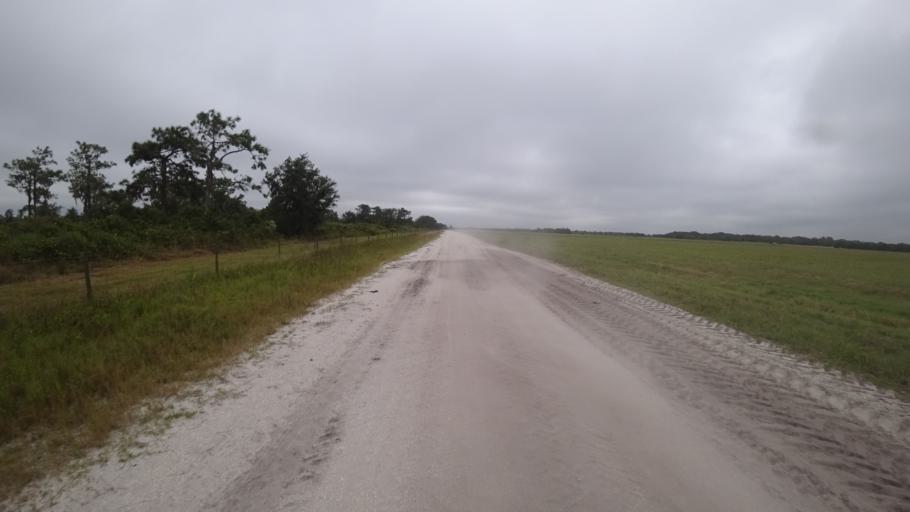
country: US
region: Florida
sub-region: Sarasota County
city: Warm Mineral Springs
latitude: 27.2903
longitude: -82.1346
